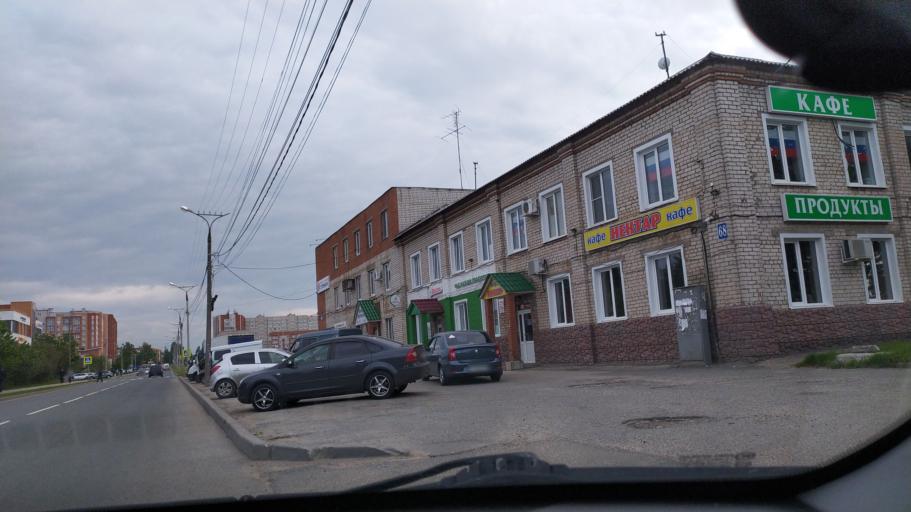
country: RU
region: Chuvashia
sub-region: Cheboksarskiy Rayon
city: Cheboksary
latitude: 56.1188
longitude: 47.2245
